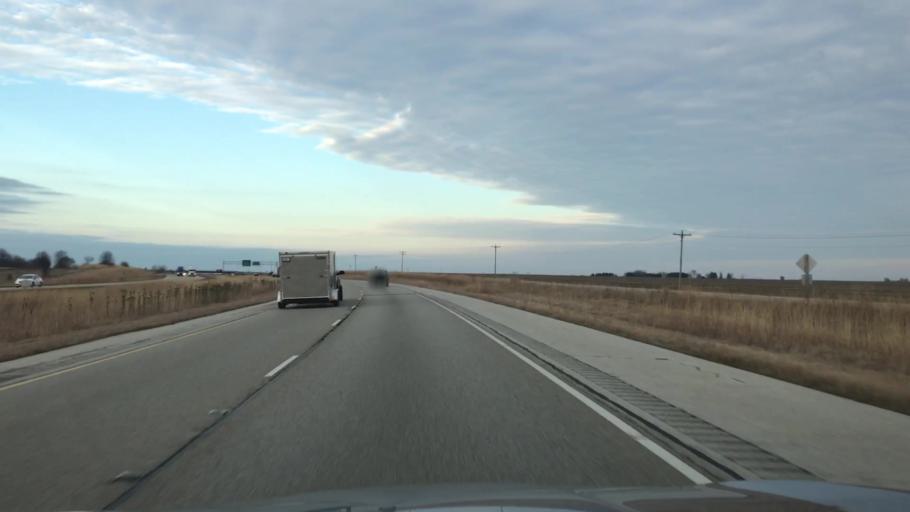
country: US
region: Illinois
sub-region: McLean County
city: Twin Grove
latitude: 40.3998
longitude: -89.0594
